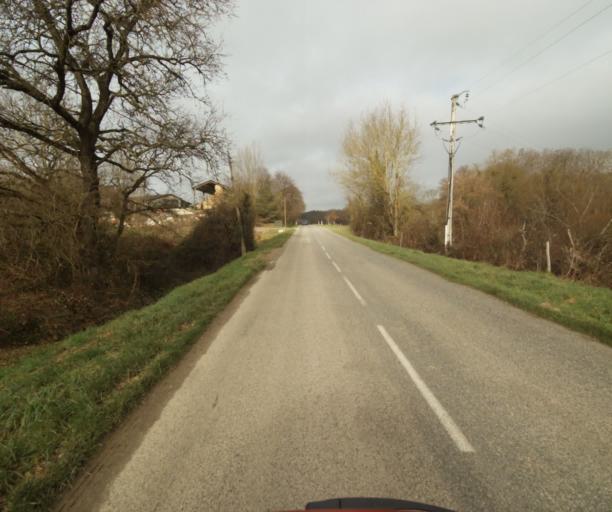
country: FR
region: Midi-Pyrenees
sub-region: Departement de l'Ariege
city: Pamiers
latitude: 43.1389
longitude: 1.5352
